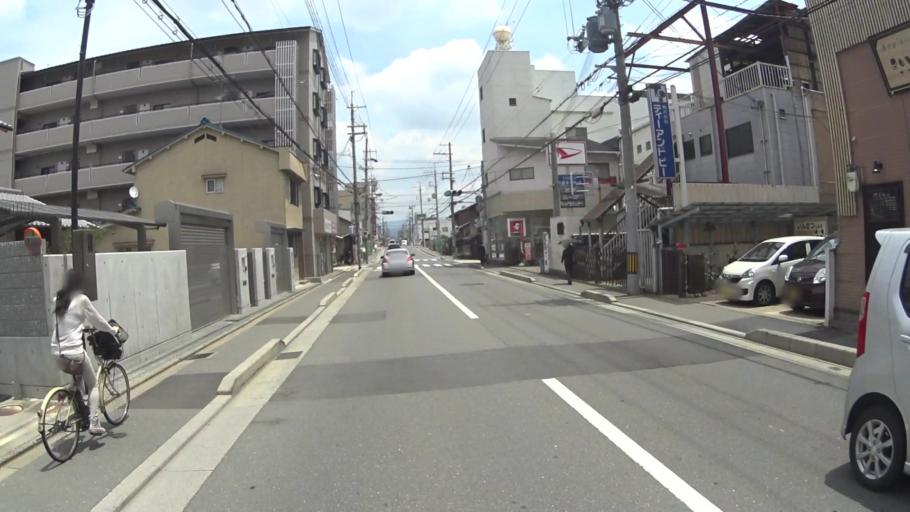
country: JP
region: Kyoto
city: Muko
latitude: 34.9841
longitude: 135.7269
